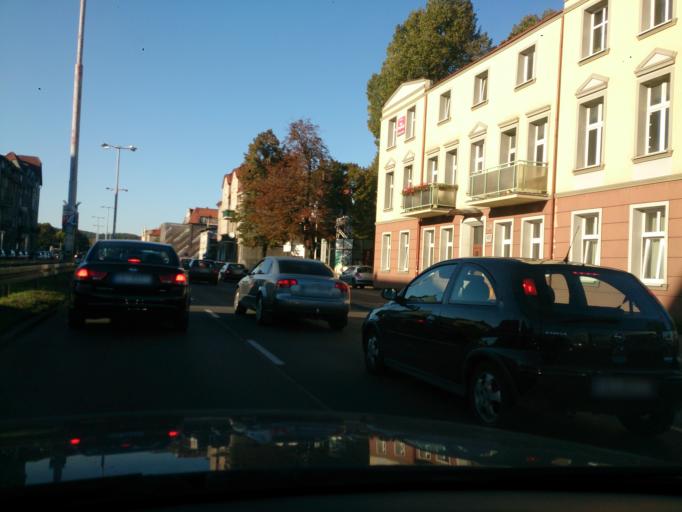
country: PL
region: Pomeranian Voivodeship
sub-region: Sopot
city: Sopot
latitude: 54.4075
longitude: 18.5694
